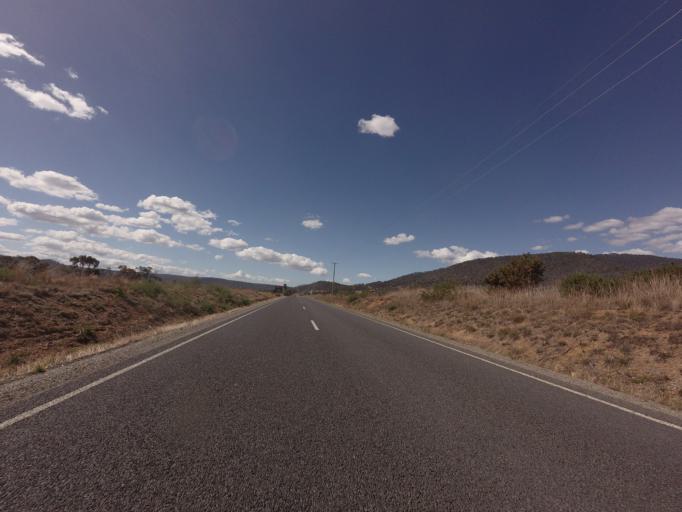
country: AU
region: Tasmania
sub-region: Break O'Day
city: St Helens
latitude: -41.6758
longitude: 147.8954
